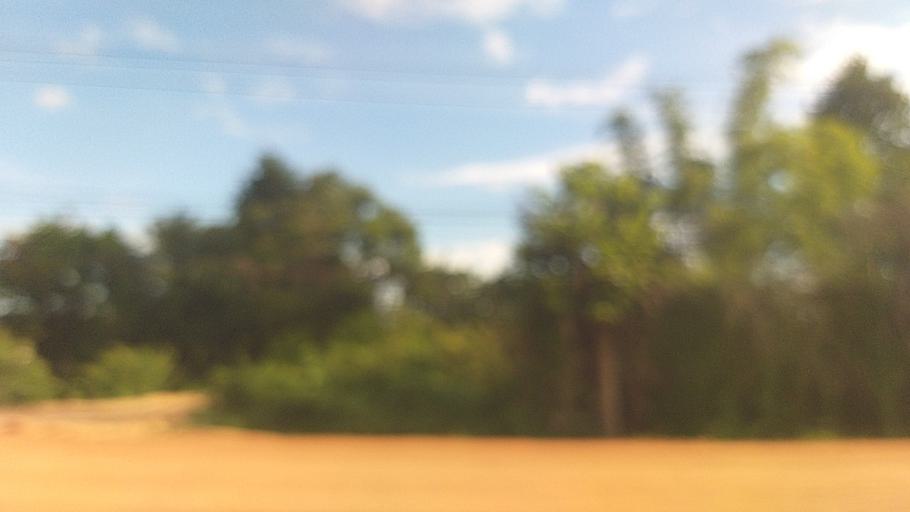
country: TH
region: Surin
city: Kap Choeng
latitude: 14.4723
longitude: 103.6092
